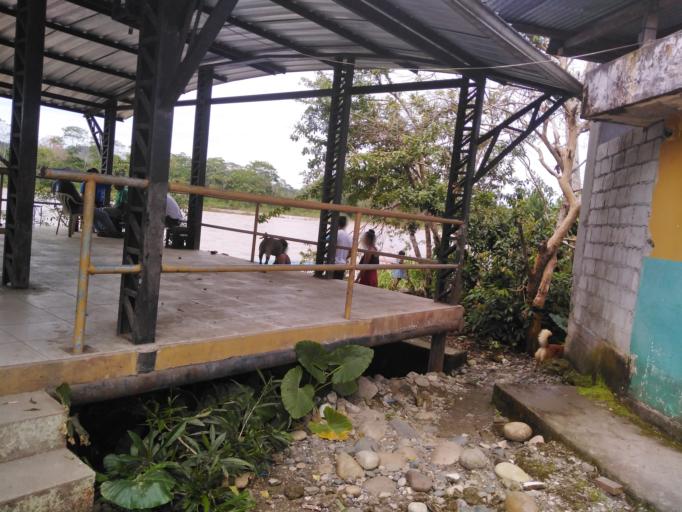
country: EC
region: Napo
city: Tena
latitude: -1.0600
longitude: -77.5459
